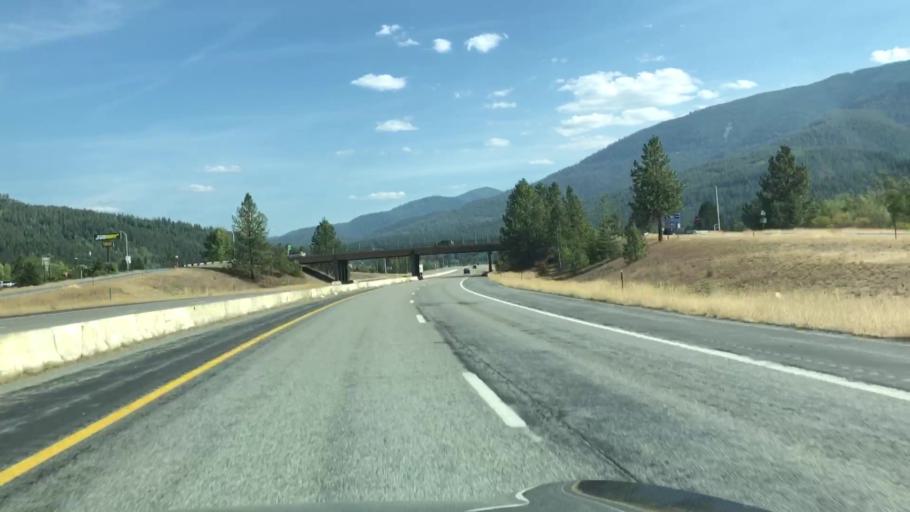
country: US
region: Idaho
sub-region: Shoshone County
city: Kellogg
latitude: 47.5470
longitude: -116.1351
